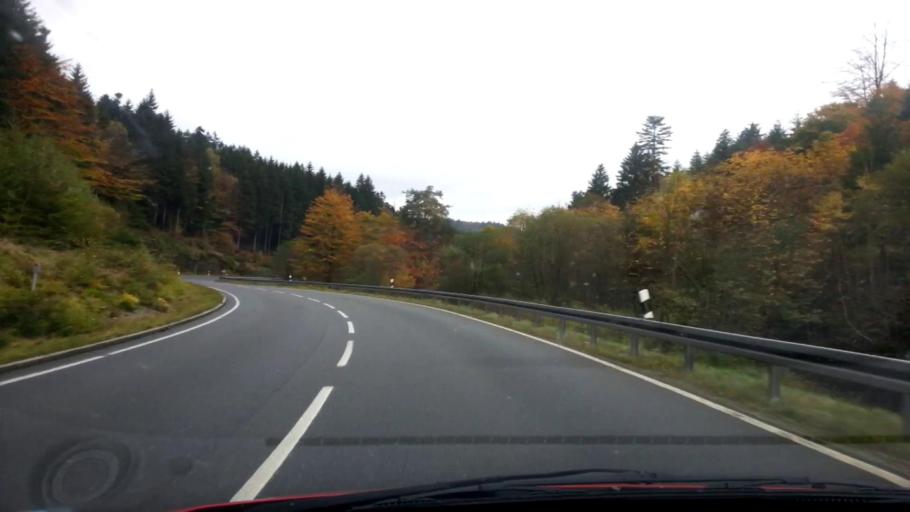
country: DE
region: Bavaria
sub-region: Upper Franconia
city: Warmensteinach
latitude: 49.9773
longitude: 11.7675
